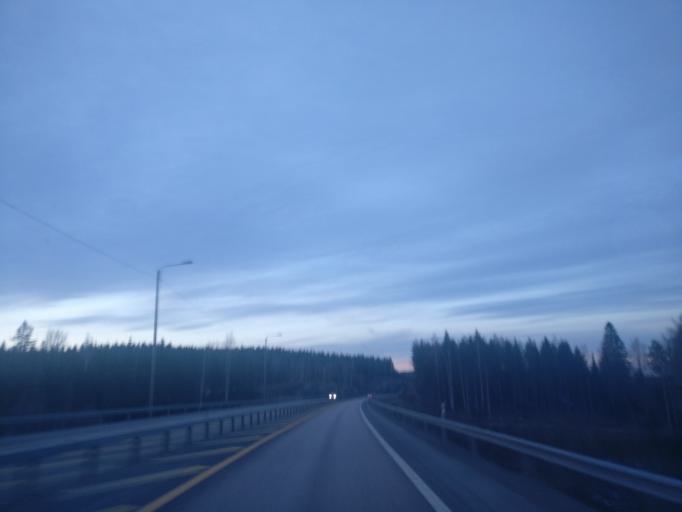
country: FI
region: Central Finland
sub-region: Jyvaeskylae
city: Saeynaetsalo
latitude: 62.2109
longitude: 25.8896
